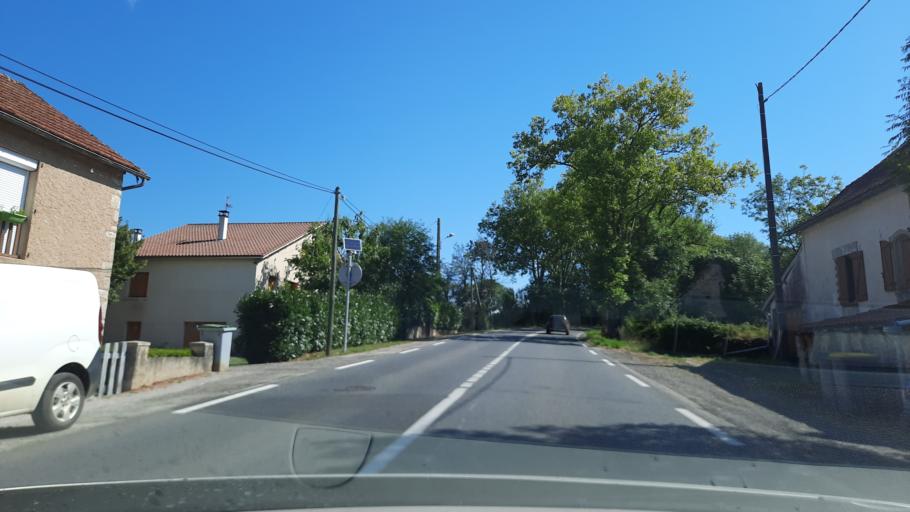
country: FR
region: Midi-Pyrenees
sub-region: Departement de l'Aveyron
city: Villefranche-de-Rouergue
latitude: 44.3222
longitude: 1.8966
